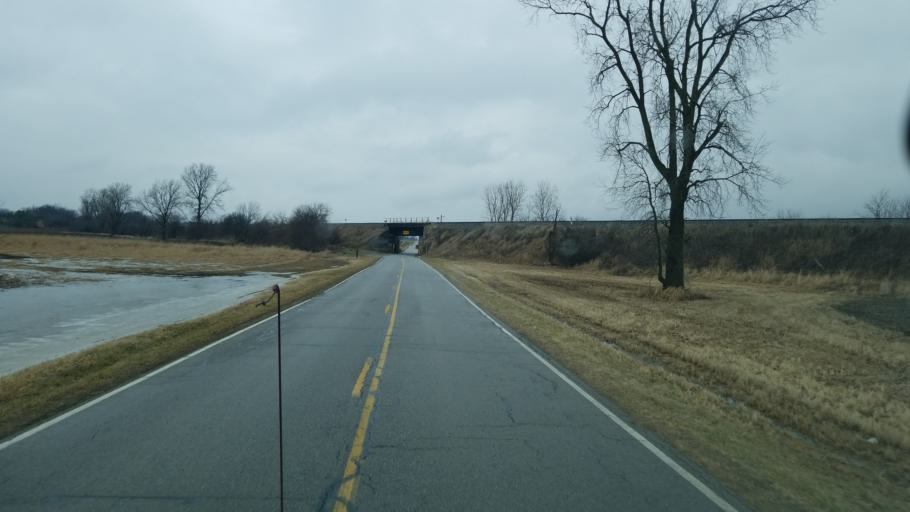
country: US
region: Ohio
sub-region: Marion County
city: Marion
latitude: 40.6323
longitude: -83.1734
